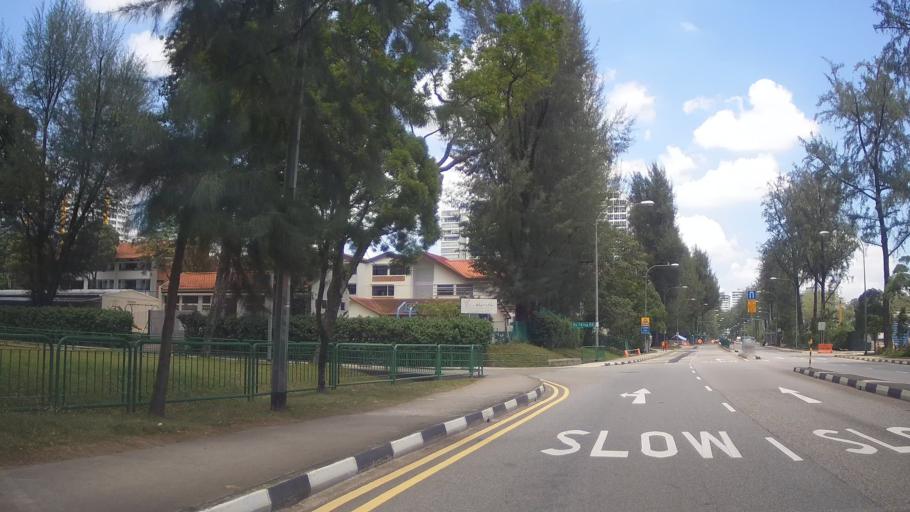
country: SG
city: Singapore
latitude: 1.3286
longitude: 103.7247
